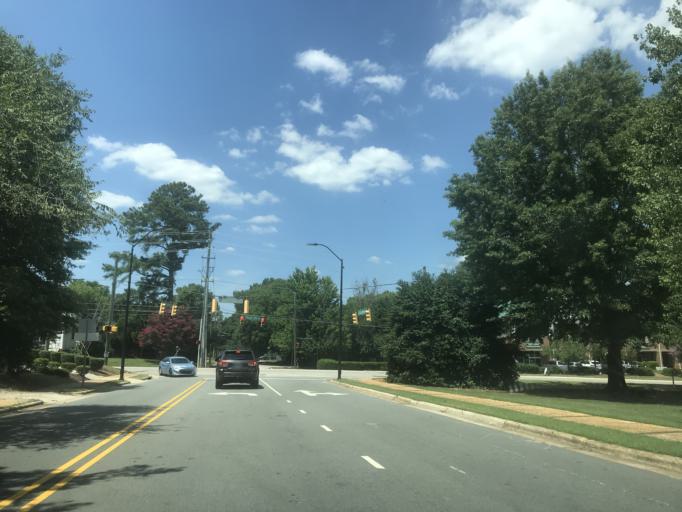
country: US
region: North Carolina
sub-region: Wake County
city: Cary
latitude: 35.7910
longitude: -78.7812
